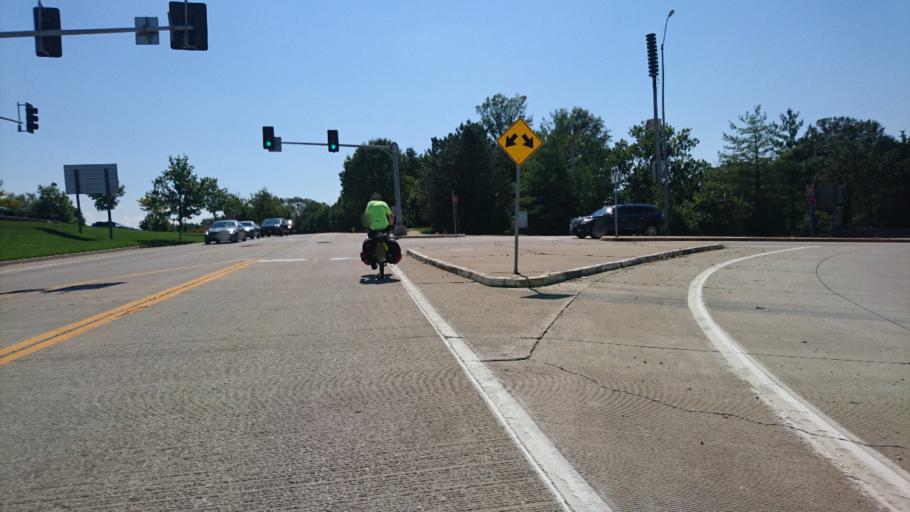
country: US
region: Missouri
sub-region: Saint Louis County
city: Town and Country
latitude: 38.6008
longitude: -90.4554
